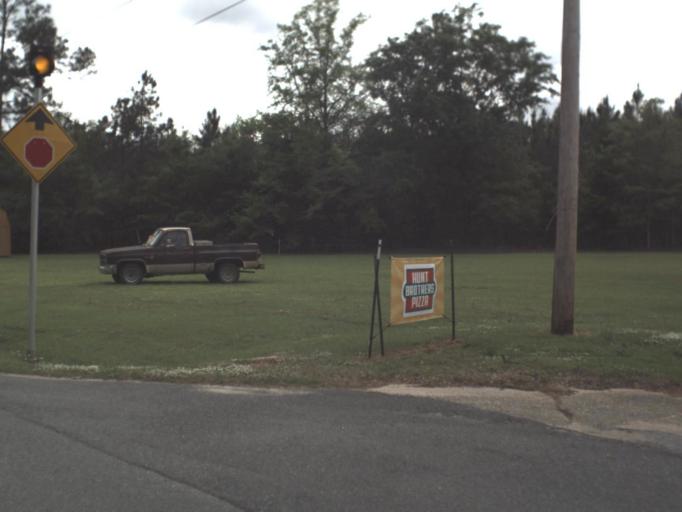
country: US
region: Alabama
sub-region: Escambia County
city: East Brewton
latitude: 30.9091
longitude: -87.0321
